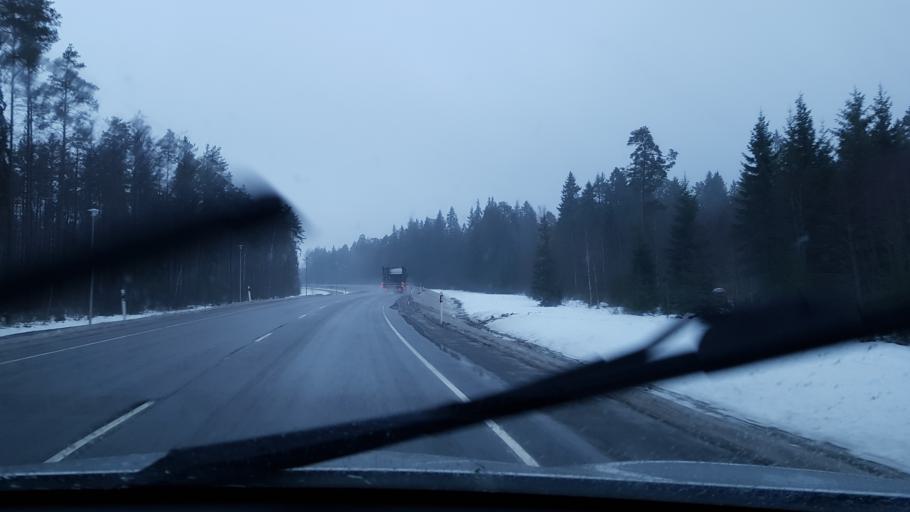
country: EE
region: Jaervamaa
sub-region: Paide linn
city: Paide
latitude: 58.8609
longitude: 25.4890
